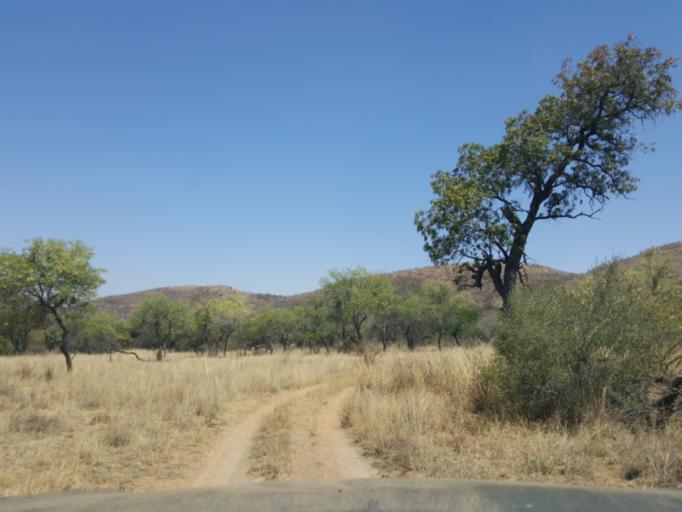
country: BW
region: South East
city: Lobatse
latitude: -25.1415
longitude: 25.6705
